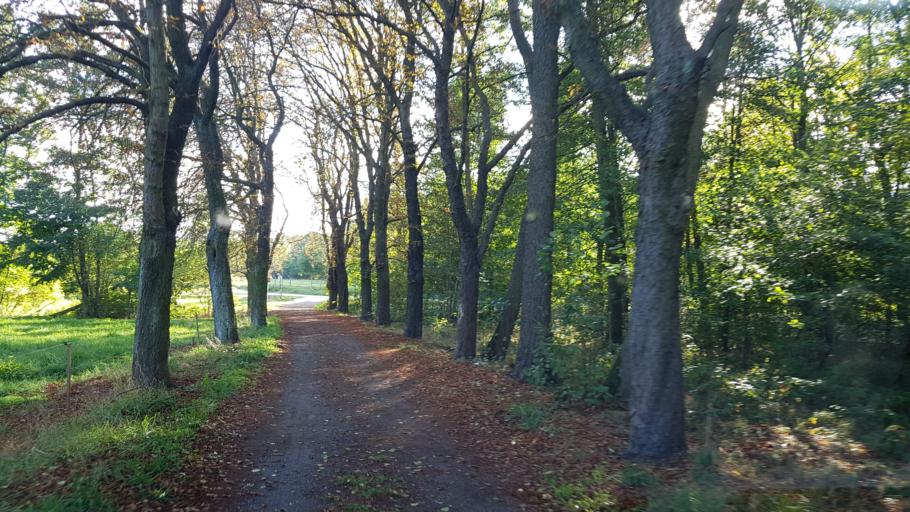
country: DE
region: Saxony
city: Dahlen
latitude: 51.3783
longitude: 12.9937
